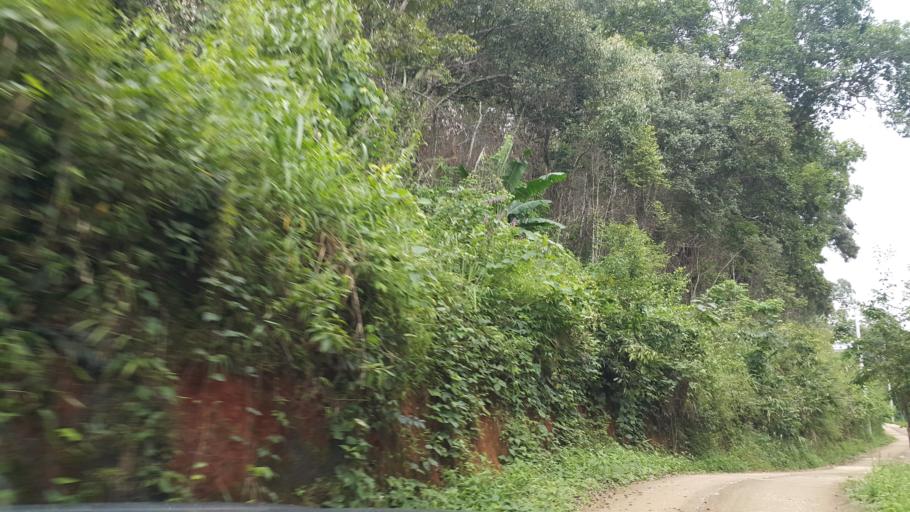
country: TH
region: Lampang
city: Wang Nuea
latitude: 19.1072
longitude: 99.3655
